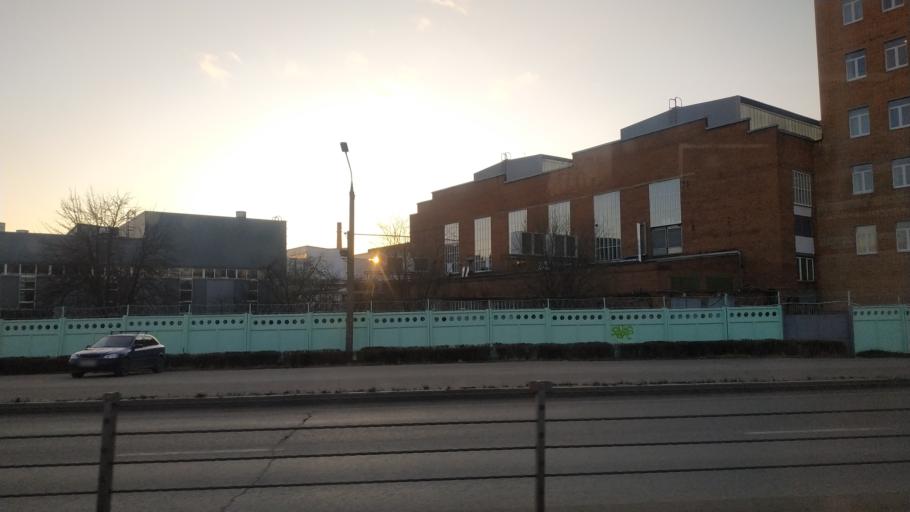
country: RU
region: Moskovskaya
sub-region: Podol'skiy Rayon
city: Podol'sk
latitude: 55.4157
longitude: 37.5770
